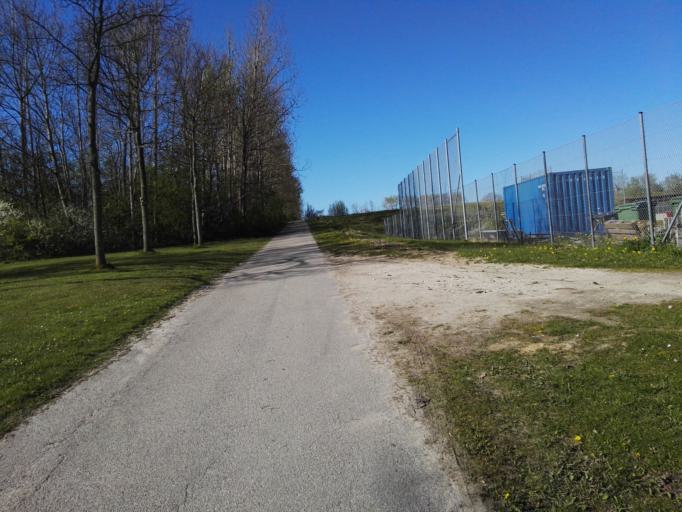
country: DK
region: Capital Region
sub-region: Egedal Kommune
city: Stenlose
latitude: 55.7577
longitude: 12.2019
